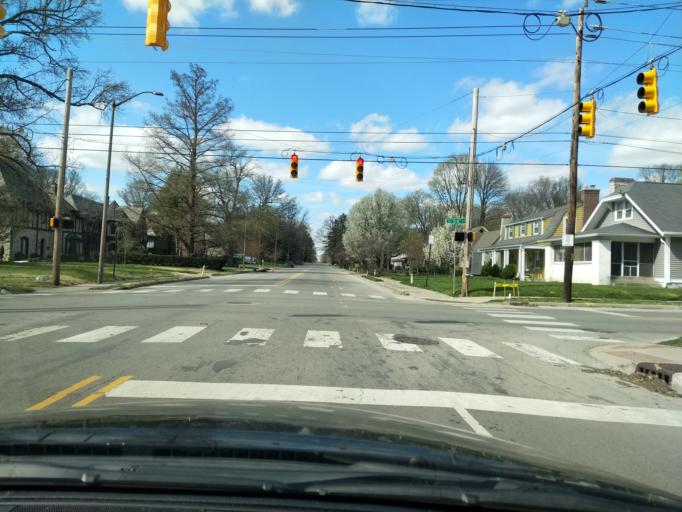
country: US
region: Indiana
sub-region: Marion County
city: Broad Ripple
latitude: 39.8509
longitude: -86.1501
